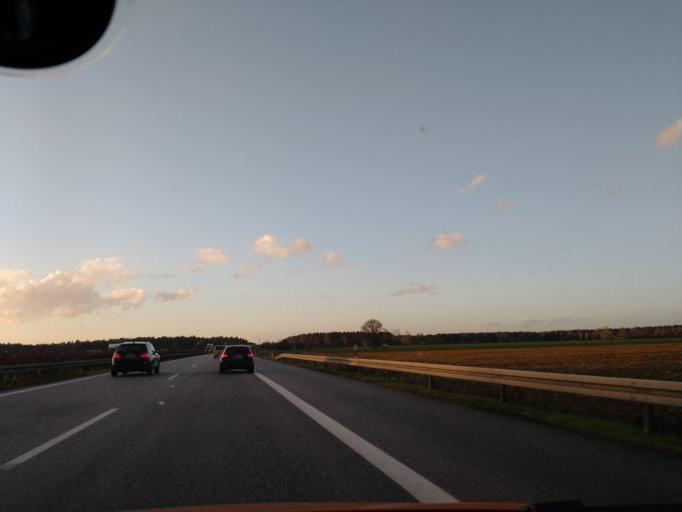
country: DE
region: Mecklenburg-Vorpommern
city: Sulstorf
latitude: 53.4742
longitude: 11.3052
